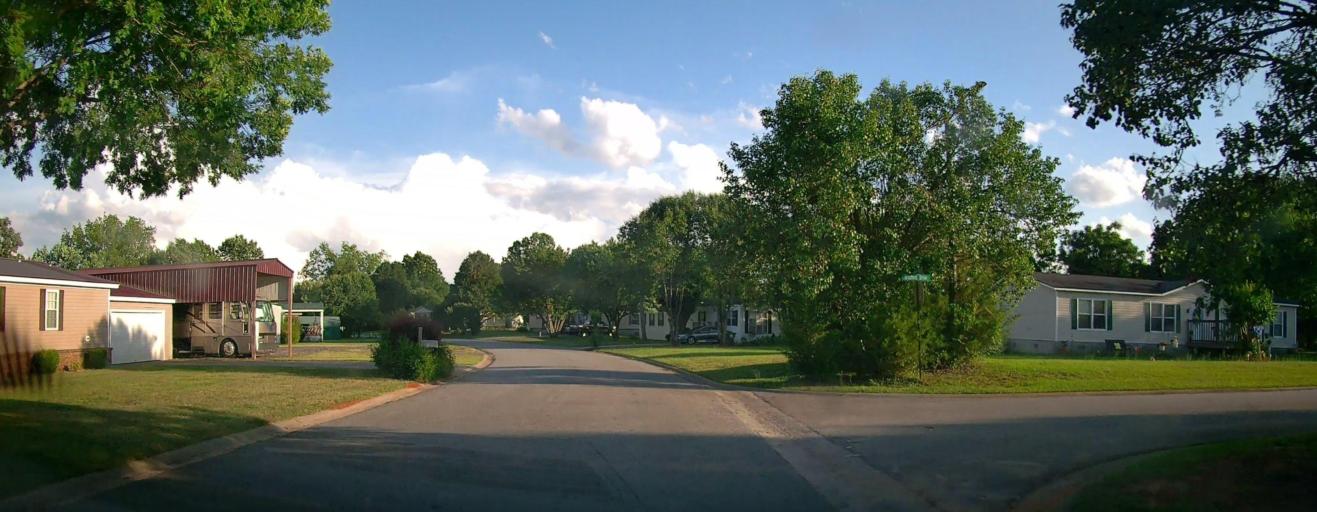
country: US
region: Georgia
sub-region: Houston County
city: Centerville
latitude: 32.6378
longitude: -83.7243
